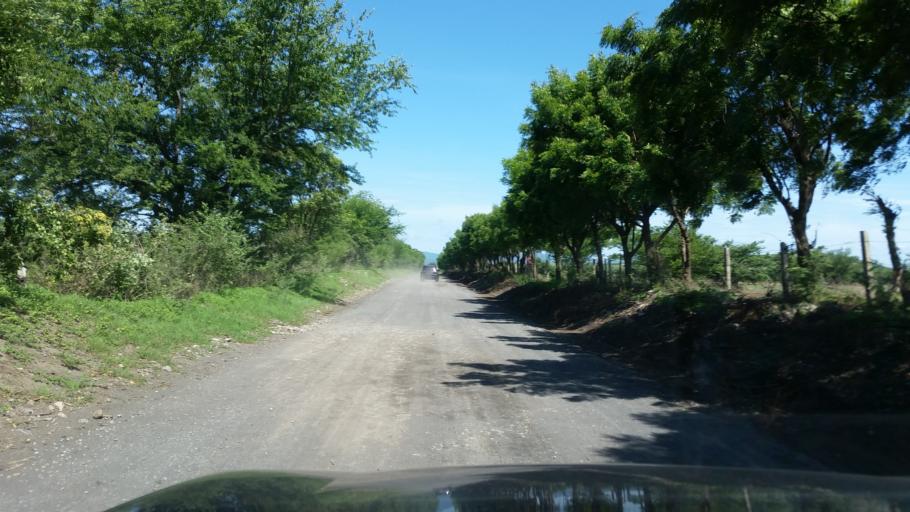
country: NI
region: Chinandega
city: Puerto Morazan
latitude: 12.7702
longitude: -87.0812
